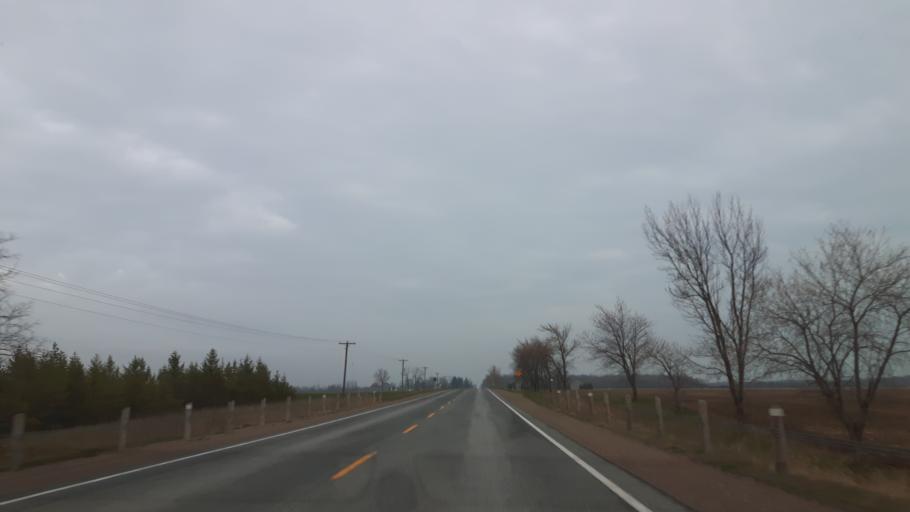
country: CA
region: Ontario
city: Bluewater
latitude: 43.5143
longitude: -81.6939
